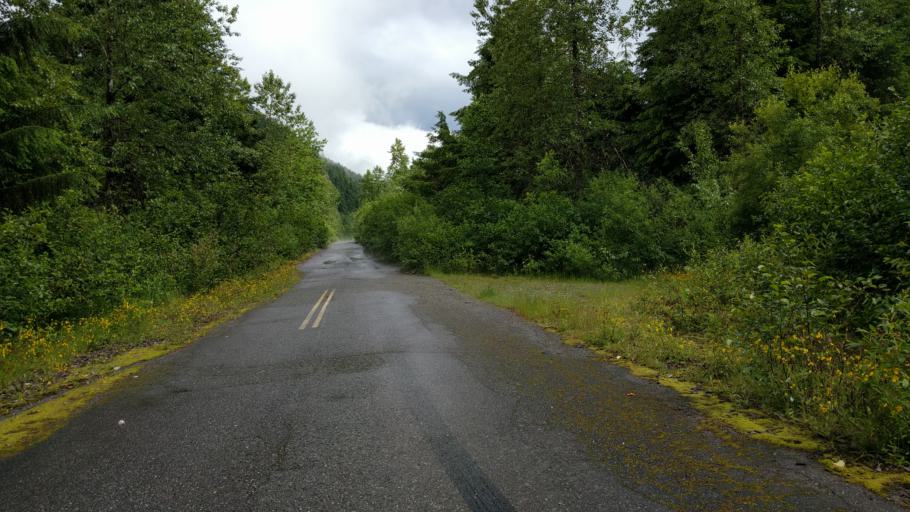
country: CA
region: British Columbia
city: Hope
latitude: 49.2936
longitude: -121.2573
